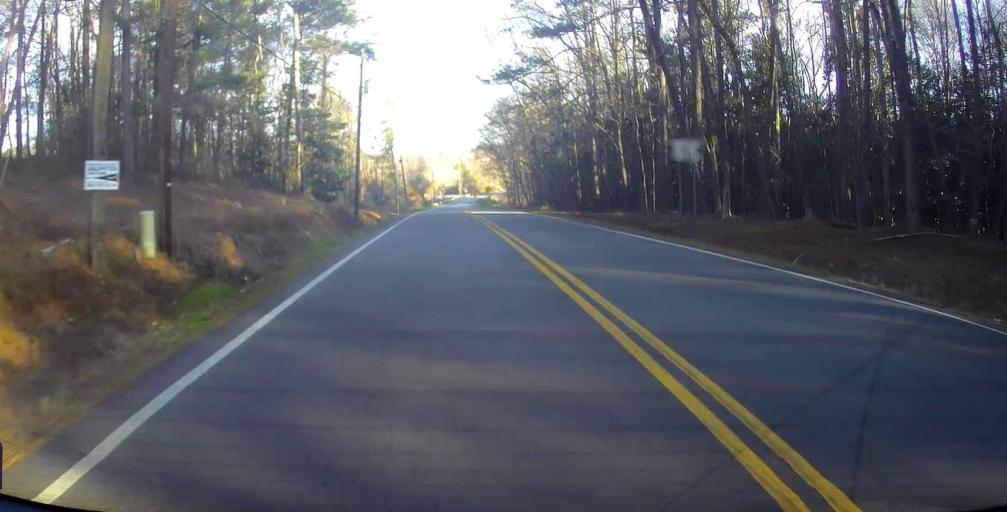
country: US
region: Georgia
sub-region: Meriwether County
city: Manchester
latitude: 32.8945
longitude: -84.6917
